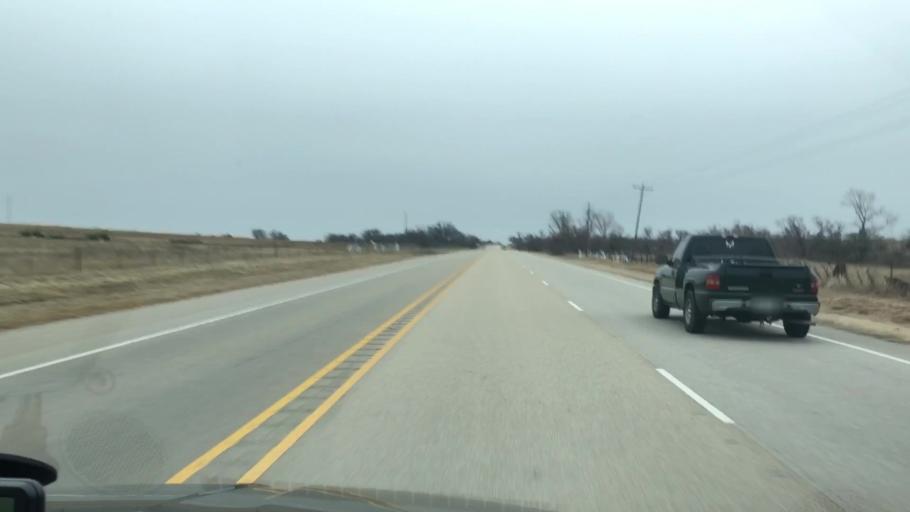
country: US
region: Texas
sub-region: Hamilton County
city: Hamilton
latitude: 31.6494
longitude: -98.1464
